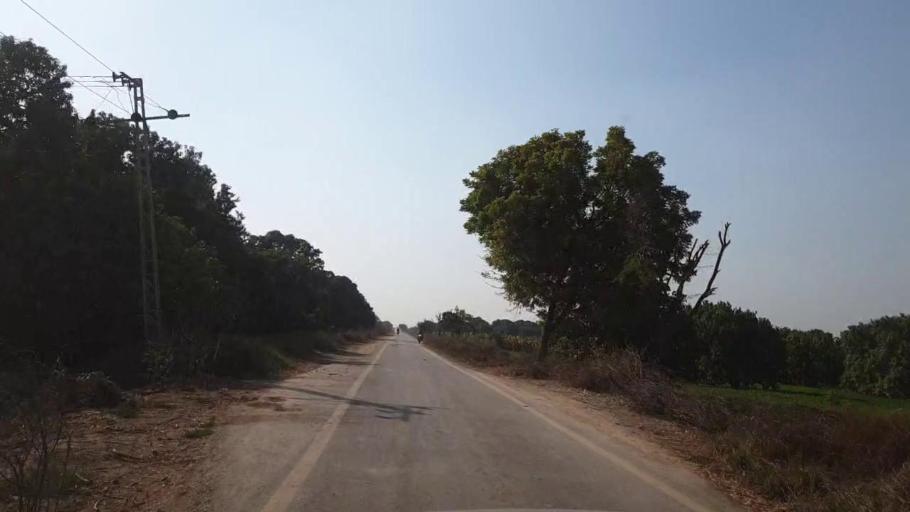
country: PK
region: Sindh
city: Tando Allahyar
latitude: 25.5689
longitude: 68.6985
